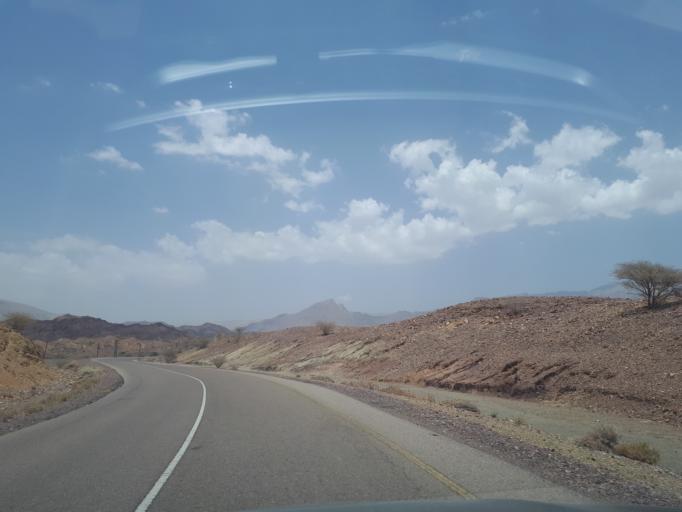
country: OM
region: Ash Sharqiyah
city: Badiyah
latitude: 22.4510
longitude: 59.0952
